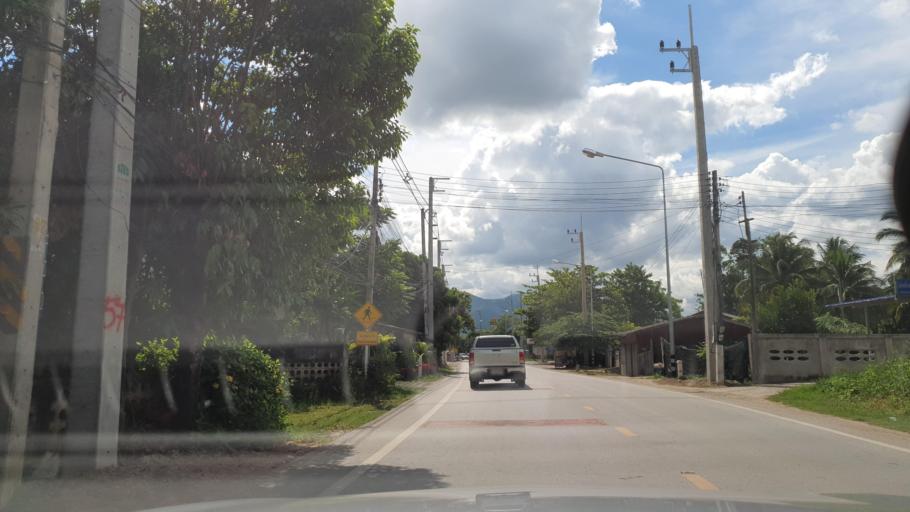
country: TH
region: Chiang Mai
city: Mae Wang
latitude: 18.6021
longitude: 98.8066
